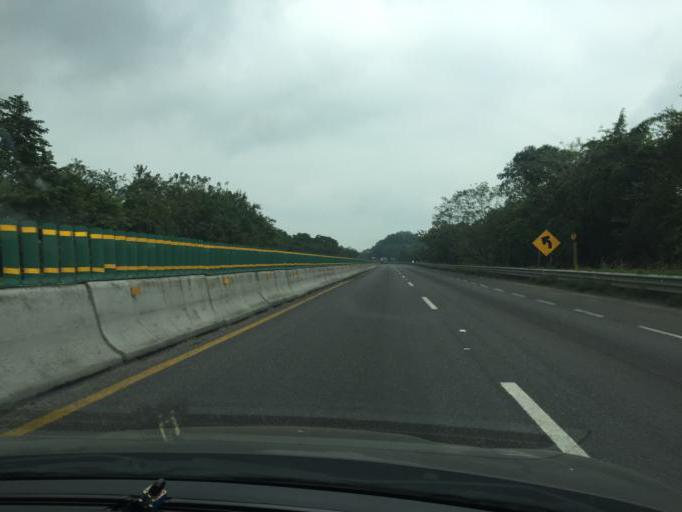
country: MX
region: Veracruz
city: Villa Nanchital
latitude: 18.0457
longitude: -94.3342
